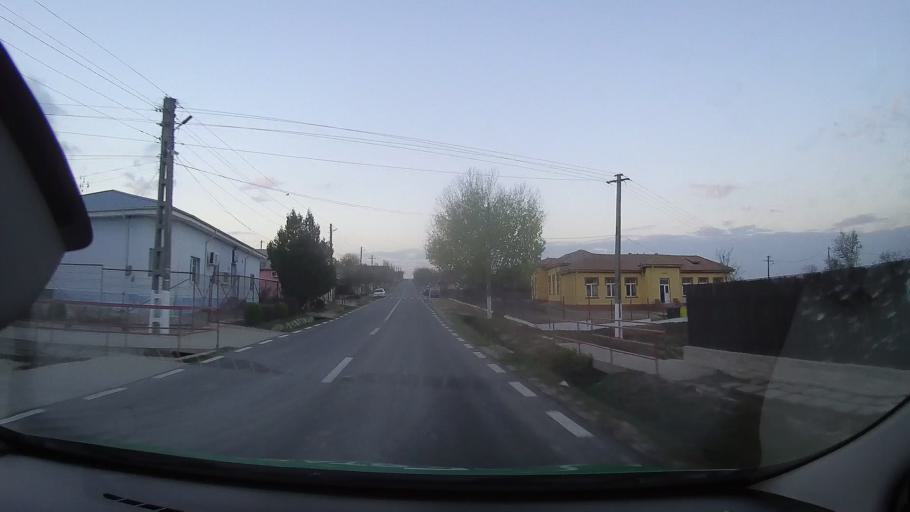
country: RO
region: Constanta
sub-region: Comuna Baneasa
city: Baneasa
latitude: 44.0994
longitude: 27.6778
